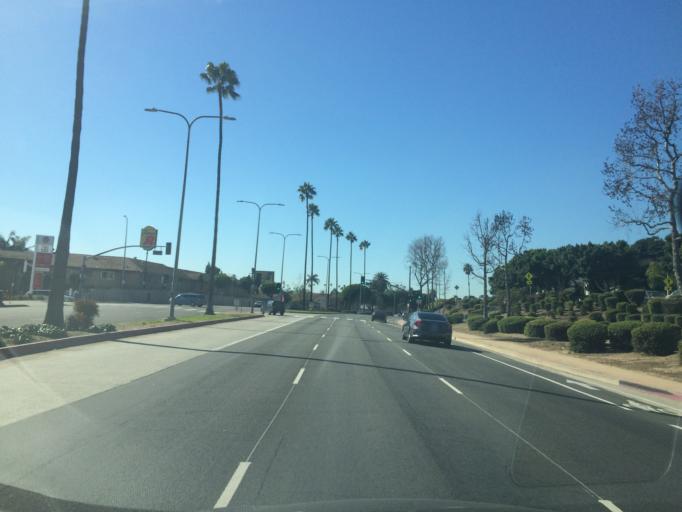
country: US
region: California
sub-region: Los Angeles County
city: South Pasadena
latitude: 34.0911
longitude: -118.1640
